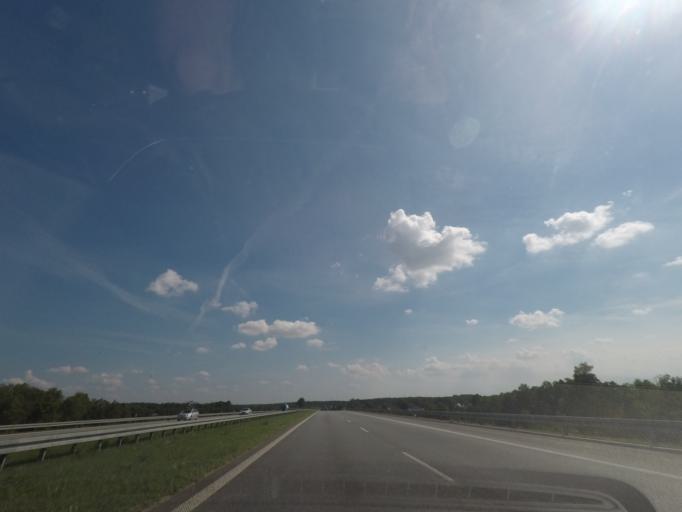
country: PL
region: Lodz Voivodeship
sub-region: Powiat lodzki wschodni
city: Andrespol
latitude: 51.7293
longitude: 19.6049
